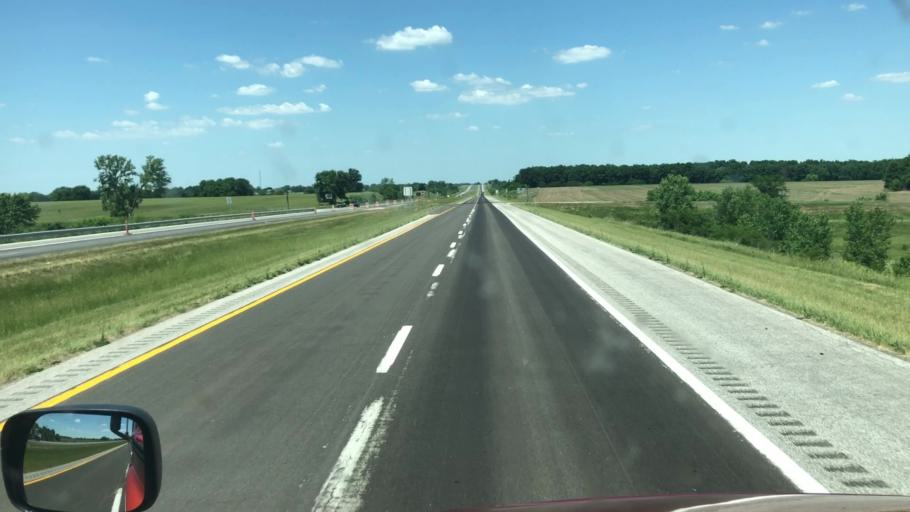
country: US
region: Missouri
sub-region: Macon County
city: La Plata
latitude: 39.9827
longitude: -92.4757
